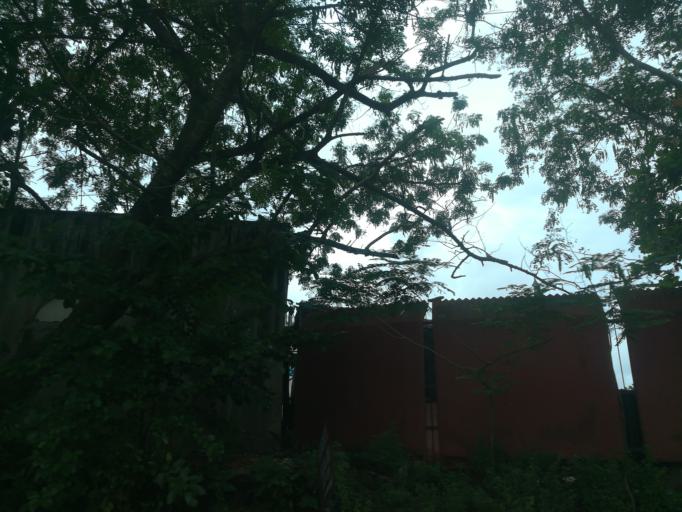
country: NG
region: Lagos
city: Lagos
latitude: 6.4407
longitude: 3.4060
